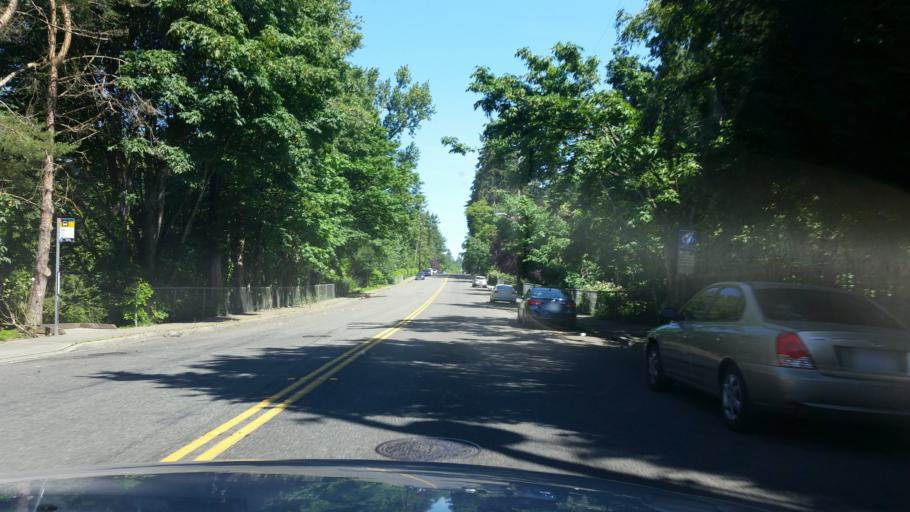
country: US
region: Washington
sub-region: Snohomish County
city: Mountlake Terrace
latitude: 47.7719
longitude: -122.3135
